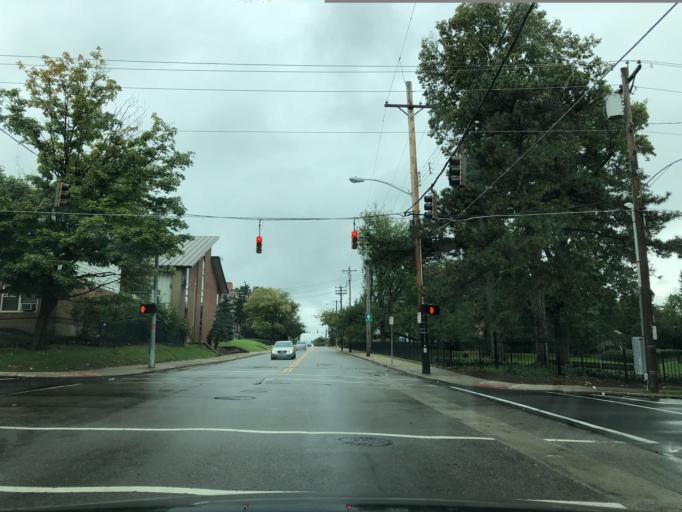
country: US
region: Ohio
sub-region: Hamilton County
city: Saint Bernard
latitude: 39.1459
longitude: -84.4948
